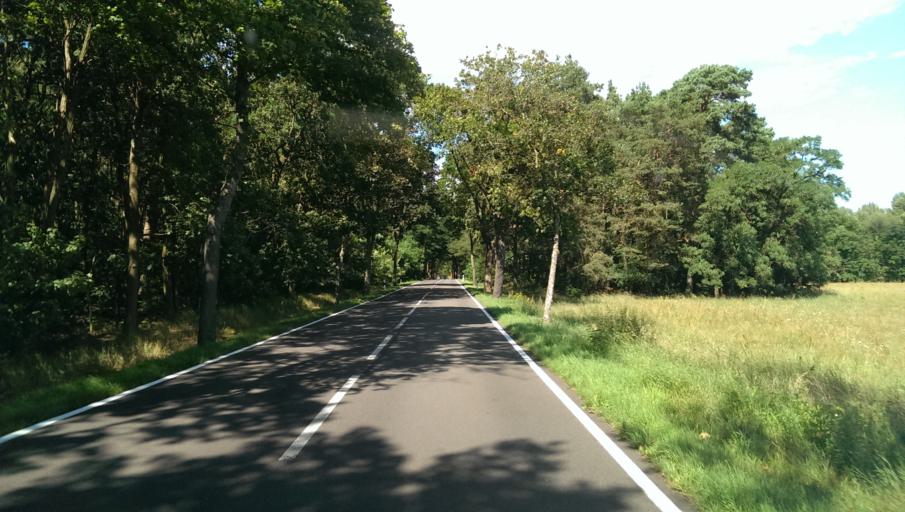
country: DE
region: Brandenburg
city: Trebbin
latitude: 52.2737
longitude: 13.1906
